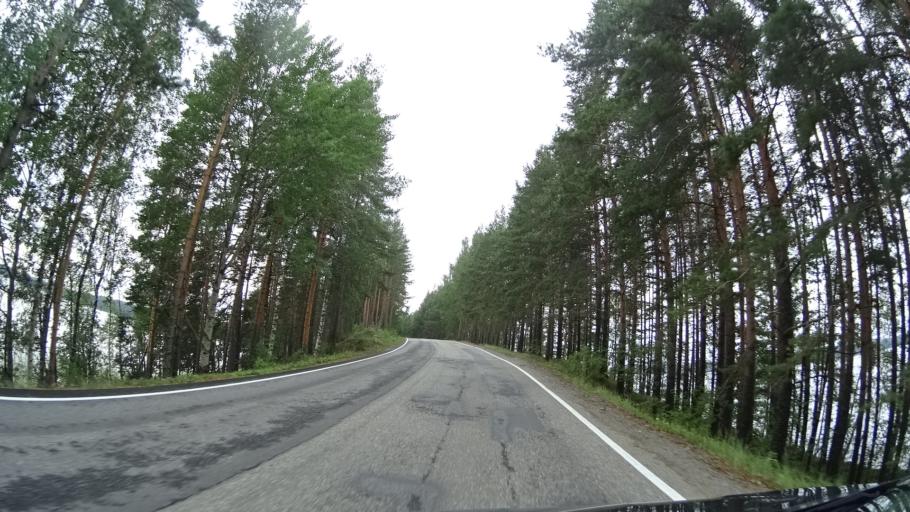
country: FI
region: Southern Savonia
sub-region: Savonlinna
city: Punkaharju
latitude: 61.7526
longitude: 29.4299
